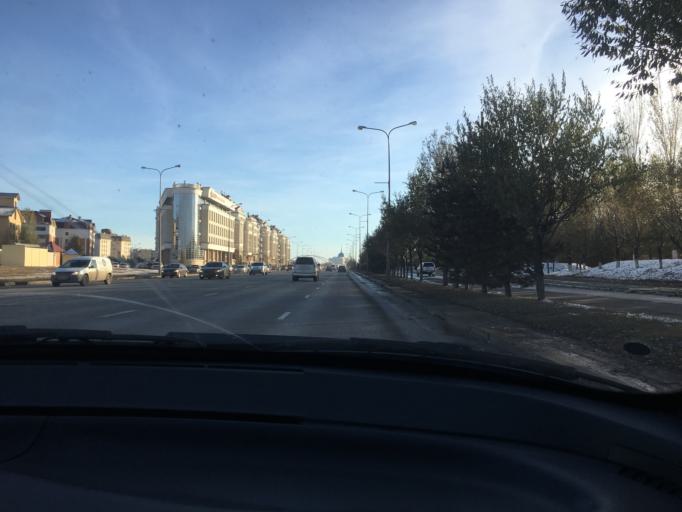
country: KZ
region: Astana Qalasy
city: Astana
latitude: 51.1465
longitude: 71.4448
